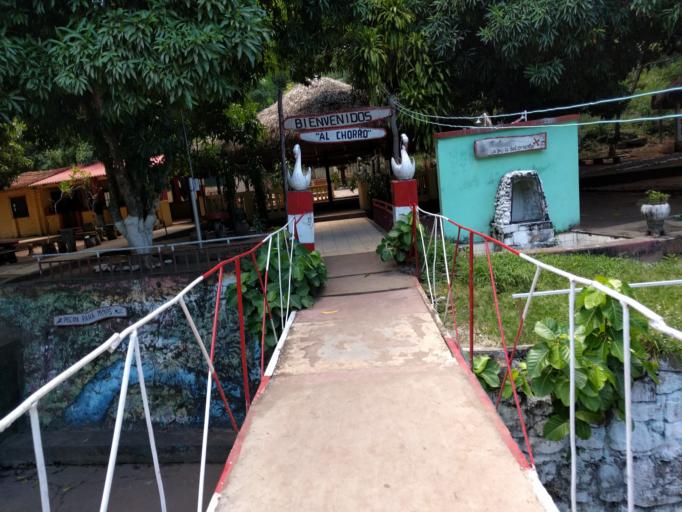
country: BO
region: Santa Cruz
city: Robore
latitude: -18.3244
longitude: -59.7500
